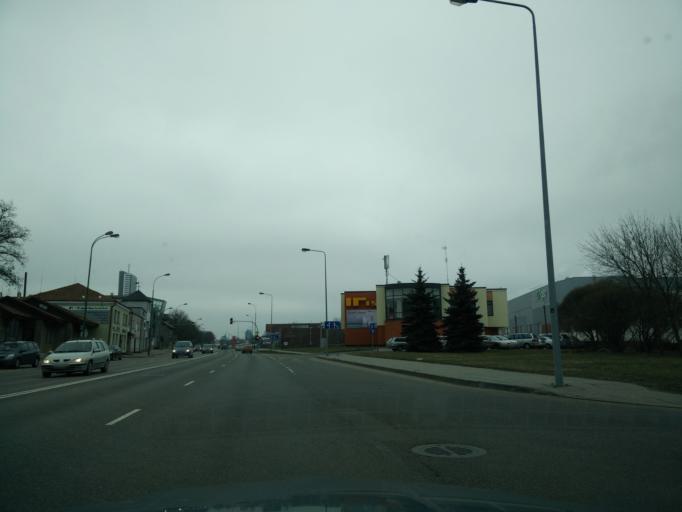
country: LT
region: Klaipedos apskritis
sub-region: Klaipeda
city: Klaipeda
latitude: 55.6972
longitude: 21.1374
